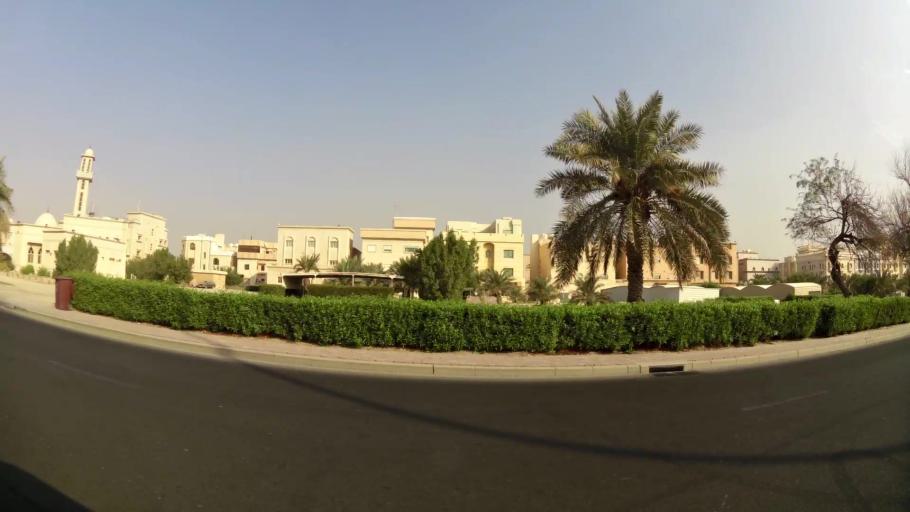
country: KW
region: Mubarak al Kabir
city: Mubarak al Kabir
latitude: 29.1806
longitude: 48.0853
